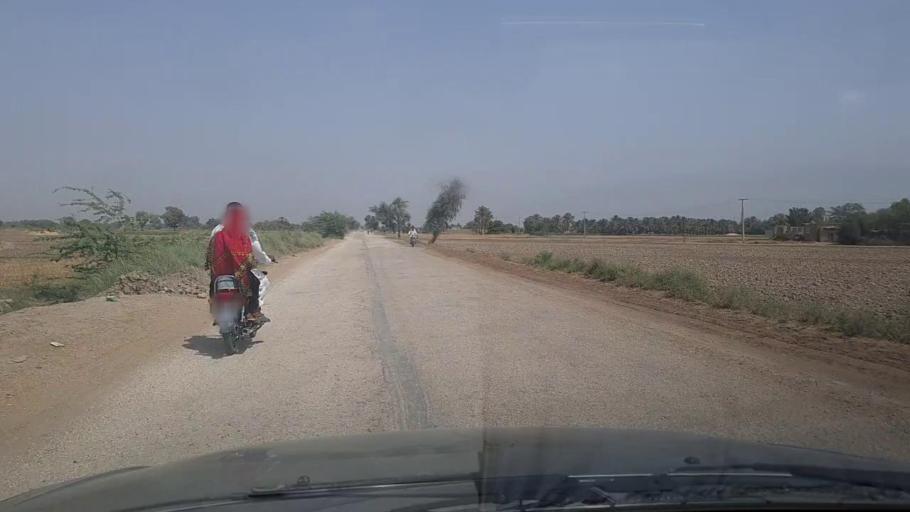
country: PK
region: Sindh
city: Setharja Old
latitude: 27.1361
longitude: 68.5297
